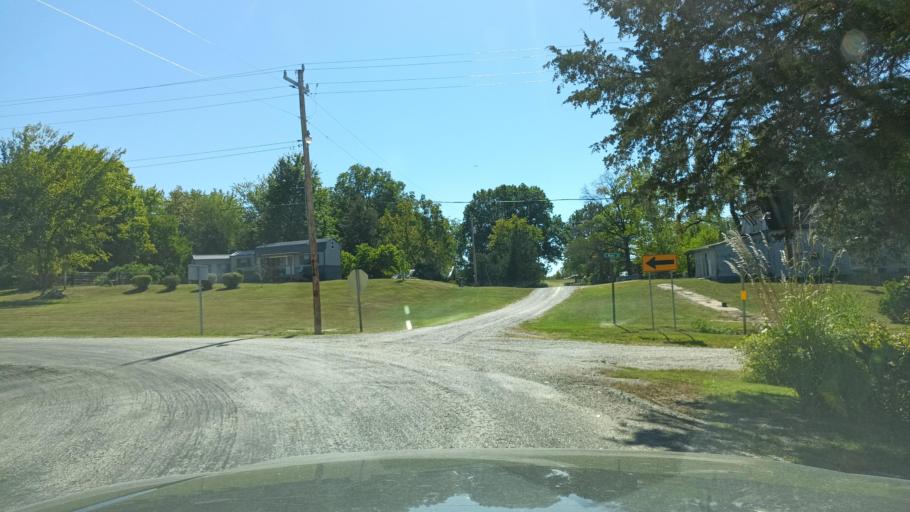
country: US
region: Missouri
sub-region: Macon County
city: La Plata
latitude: 39.9556
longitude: -92.6498
